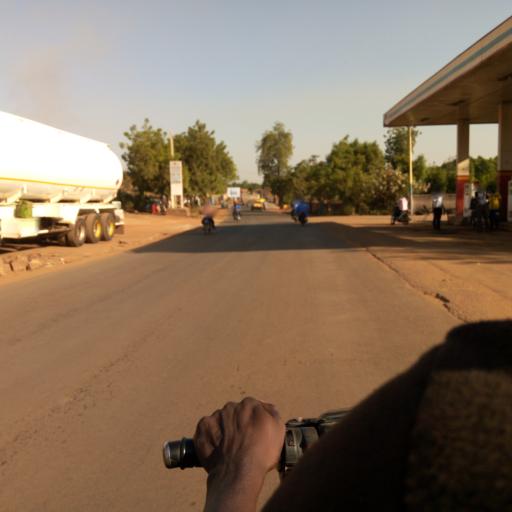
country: ML
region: Bamako
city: Bamako
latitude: 12.6601
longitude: -8.0339
